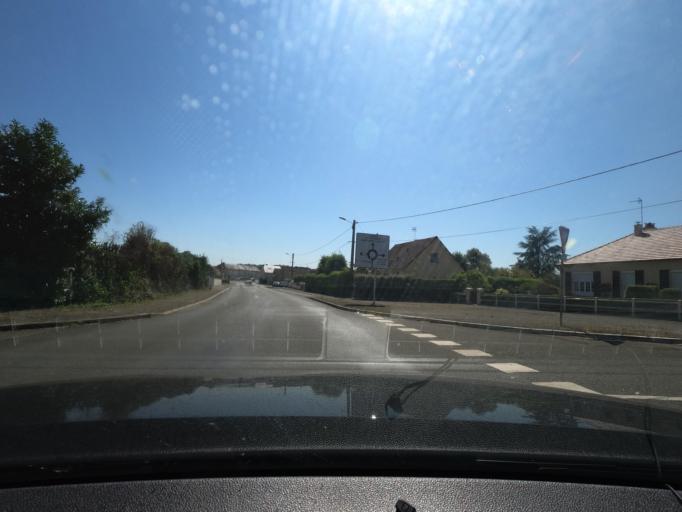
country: FR
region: Pays de la Loire
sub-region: Departement de la Sarthe
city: Saint-Cosme-en-Vairais
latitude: 48.2749
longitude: 0.4562
